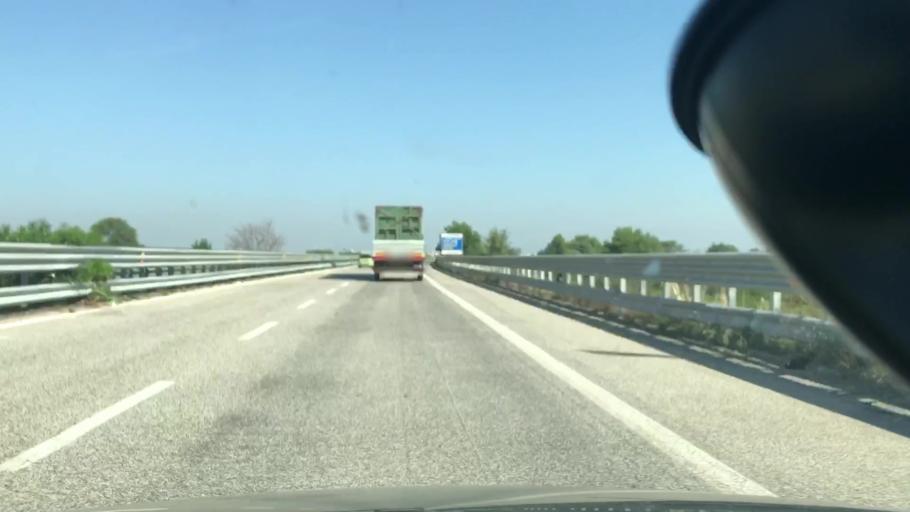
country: IT
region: Apulia
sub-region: Provincia di Foggia
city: Foggia
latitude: 41.4175
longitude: 15.5586
